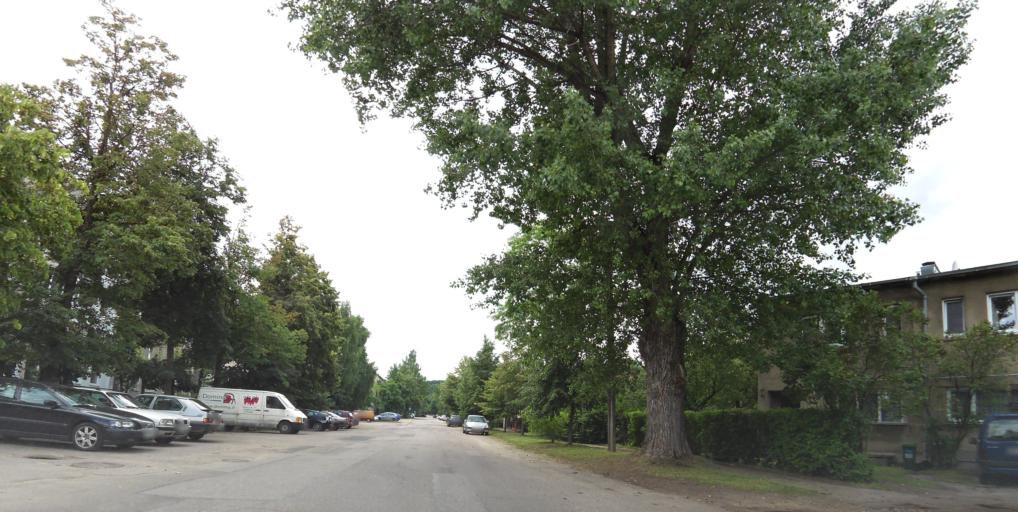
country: LT
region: Vilnius County
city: Seskine
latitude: 54.7009
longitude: 25.2473
